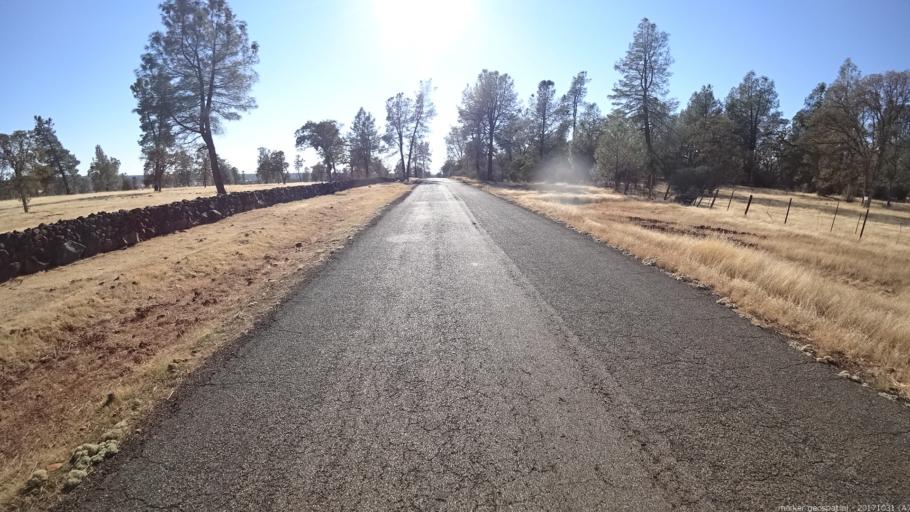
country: US
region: California
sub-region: Shasta County
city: Palo Cedro
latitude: 40.4707
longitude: -122.0915
